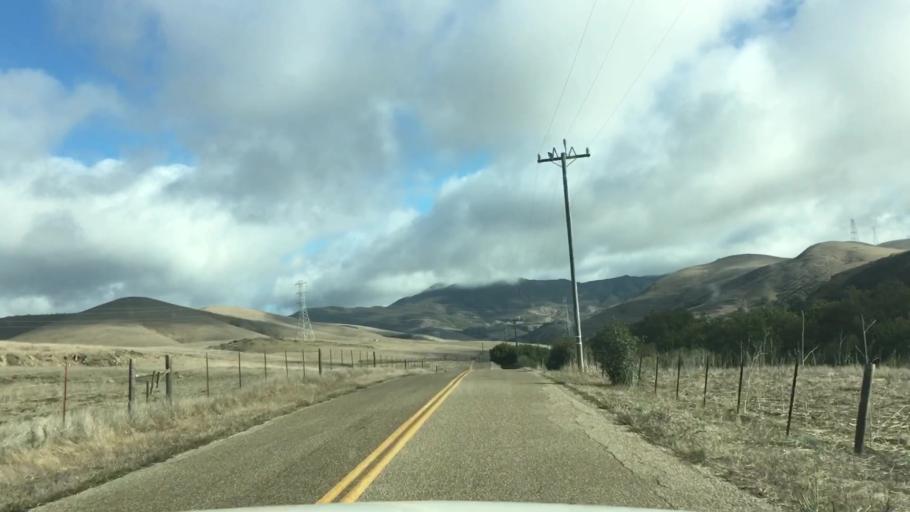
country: US
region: California
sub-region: San Luis Obispo County
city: Morro Bay
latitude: 35.3746
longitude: -120.7964
